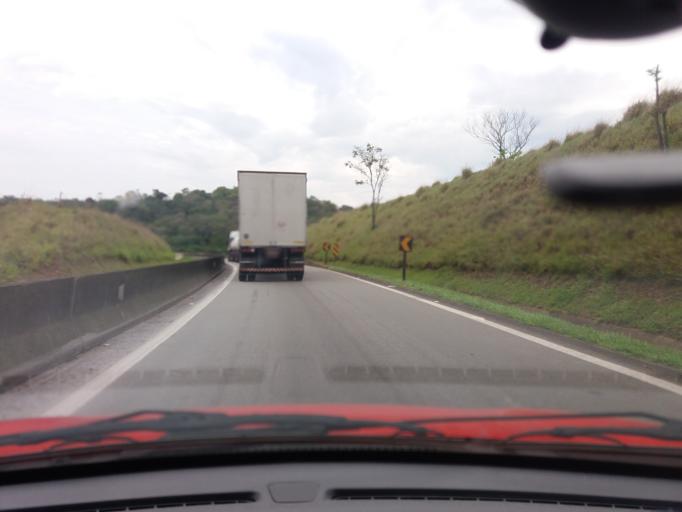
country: BR
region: Sao Paulo
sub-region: Caieiras
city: Caieiras
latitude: -23.4362
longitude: -46.7609
